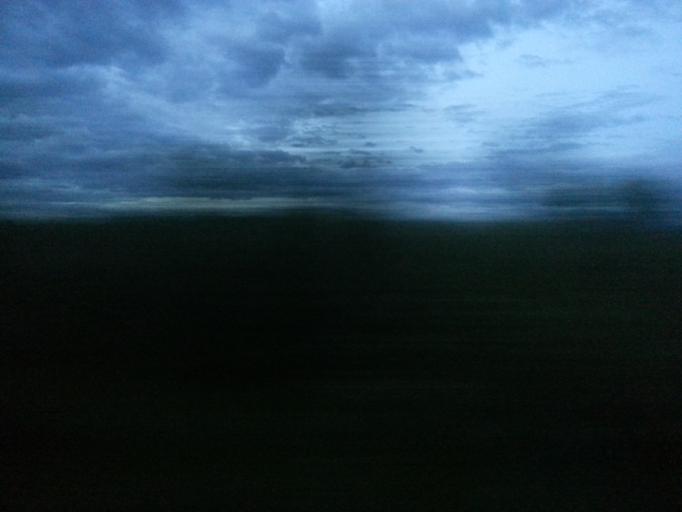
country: NO
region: Akershus
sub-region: Ullensaker
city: Klofta
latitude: 60.0648
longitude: 11.1405
